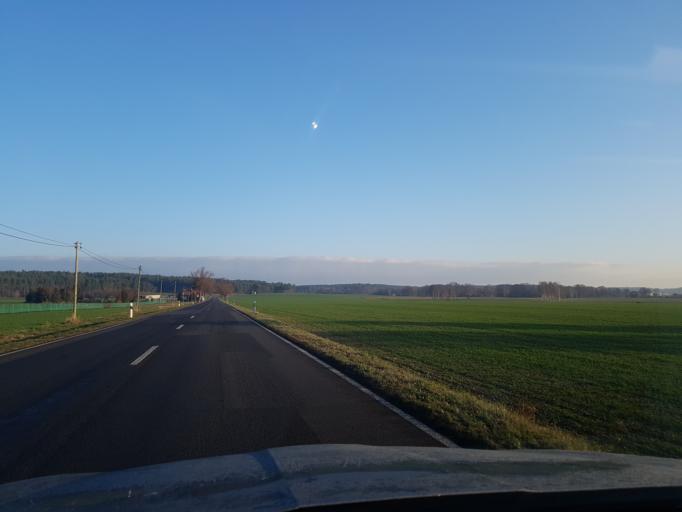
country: DE
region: Brandenburg
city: Schlieben
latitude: 51.7321
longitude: 13.4236
